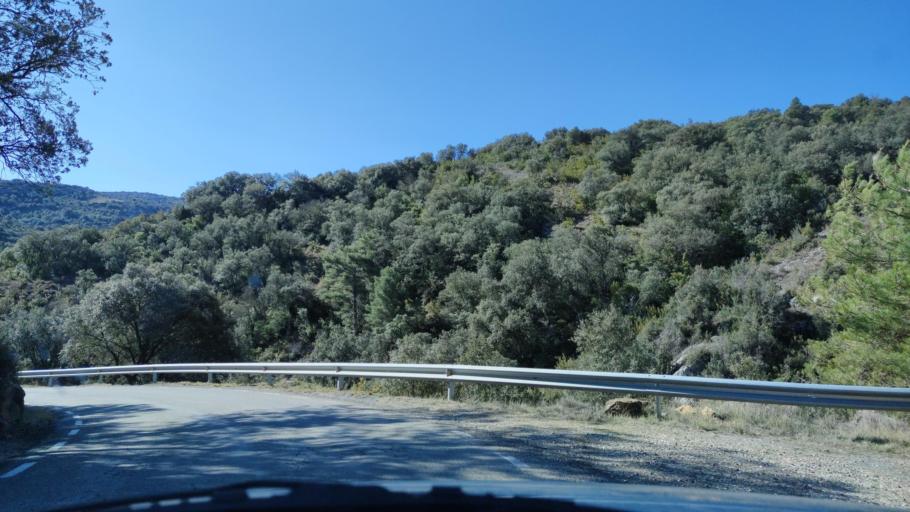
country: ES
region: Catalonia
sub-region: Provincia de Lleida
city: Artesa de Segre
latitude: 42.0125
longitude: 1.0295
